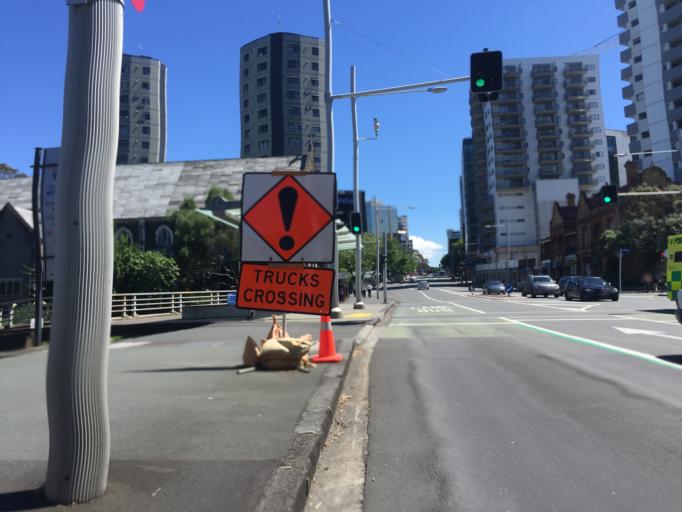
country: NZ
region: Auckland
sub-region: Auckland
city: Auckland
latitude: -36.8540
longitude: 174.7682
